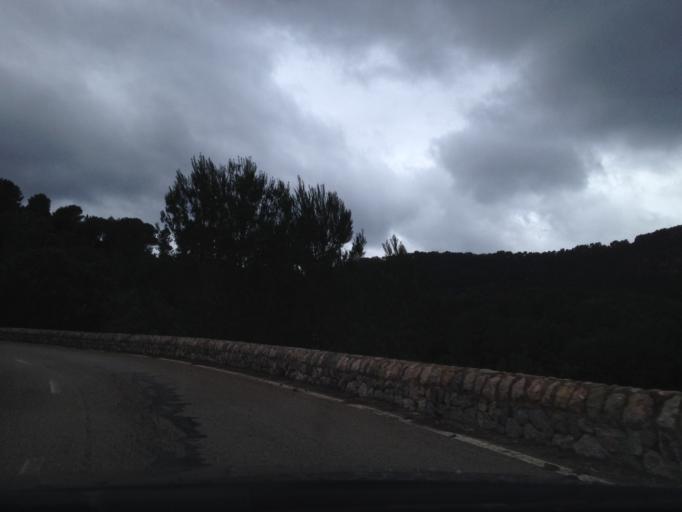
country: ES
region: Balearic Islands
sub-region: Illes Balears
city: Soller
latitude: 39.7756
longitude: 2.6954
